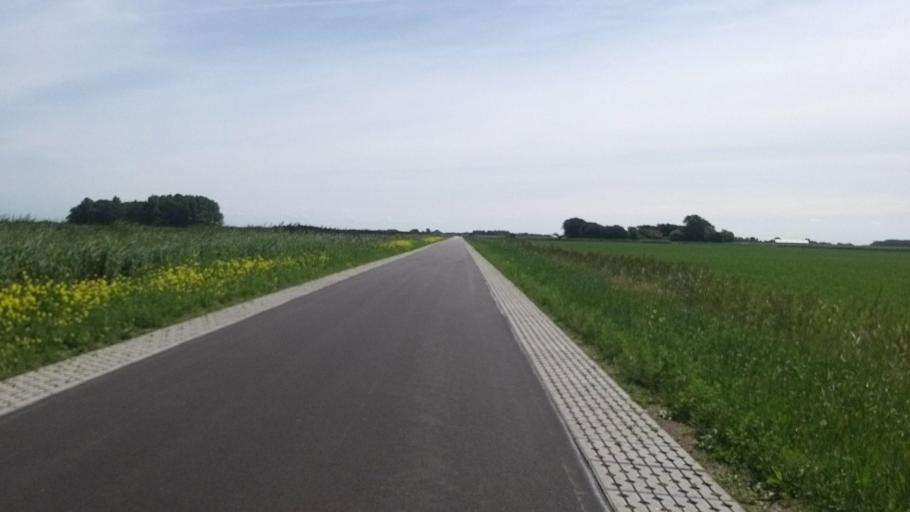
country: NL
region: North Holland
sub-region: Gemeente Texel
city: Den Burg
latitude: 53.1080
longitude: 4.8305
